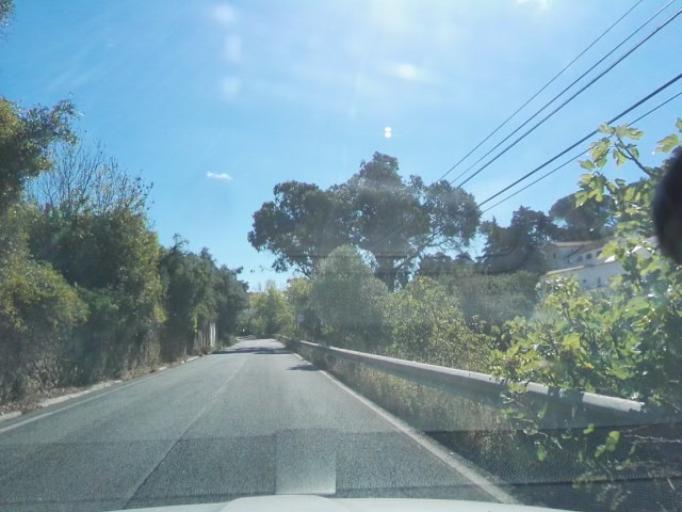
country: PT
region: Lisbon
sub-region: Vila Franca de Xira
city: Sao Joao dos Montes
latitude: 38.9420
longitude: -9.0325
